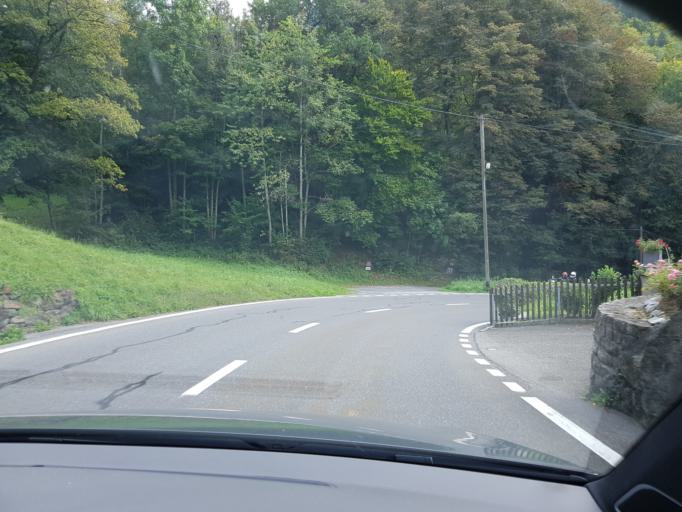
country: CH
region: Bern
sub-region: Interlaken-Oberhasli District
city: Meiringen
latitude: 46.7073
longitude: 8.2361
